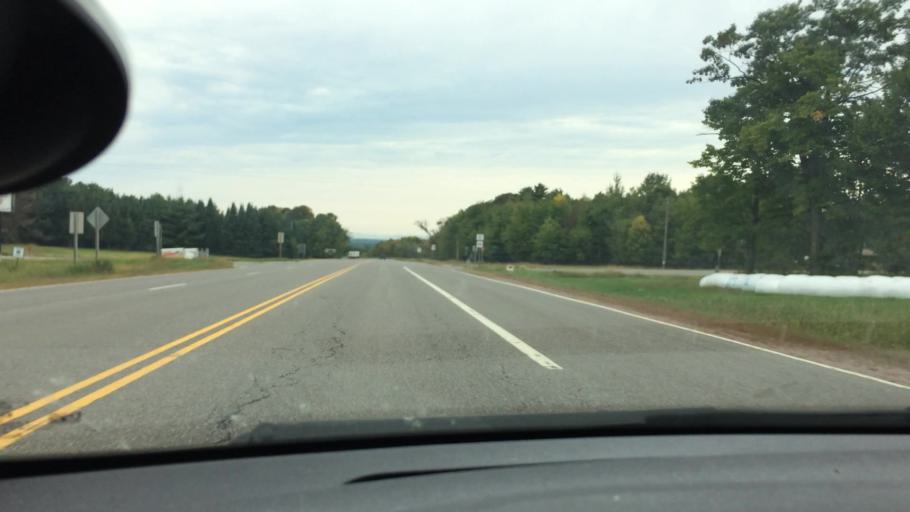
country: US
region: Wisconsin
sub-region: Clark County
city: Neillsville
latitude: 44.5645
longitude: -90.6583
